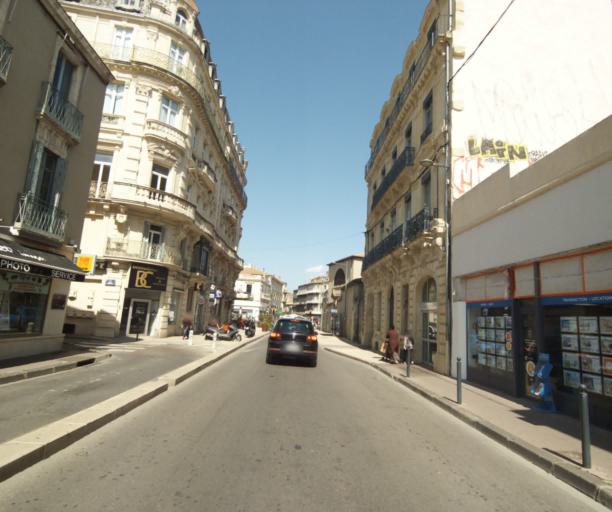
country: FR
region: Languedoc-Roussillon
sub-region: Departement de l'Herault
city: Montpellier
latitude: 43.6048
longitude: 3.8741
